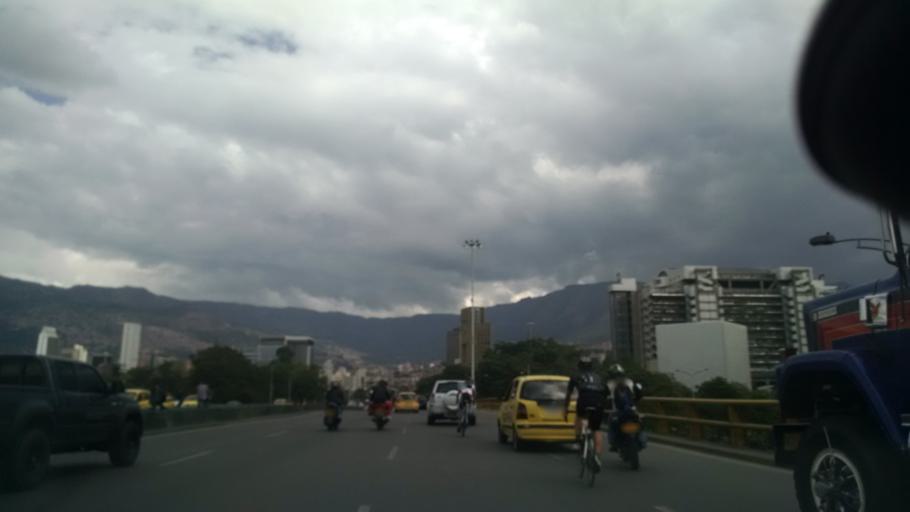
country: CO
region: Antioquia
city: Medellin
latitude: 6.2481
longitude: -75.5807
